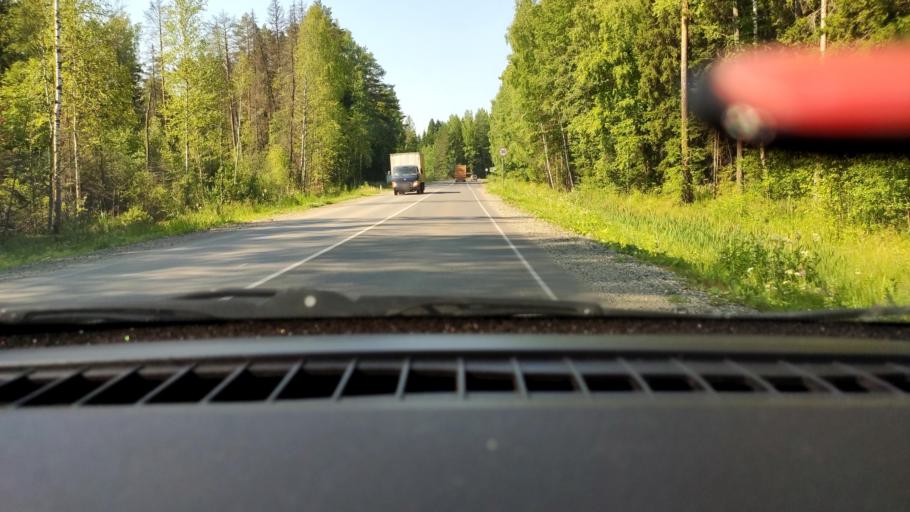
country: RU
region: Perm
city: Nytva
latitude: 57.9312
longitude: 55.4899
